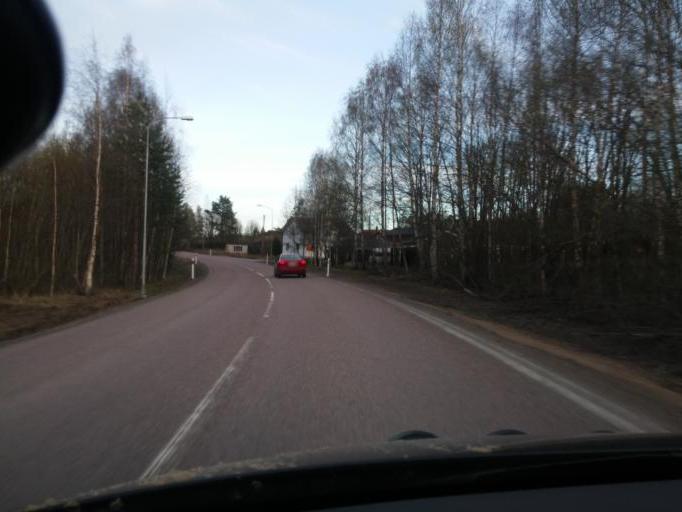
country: SE
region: Gaevleborg
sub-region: Ljusdals Kommun
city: Ljusdal
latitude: 61.8381
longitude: 16.0030
